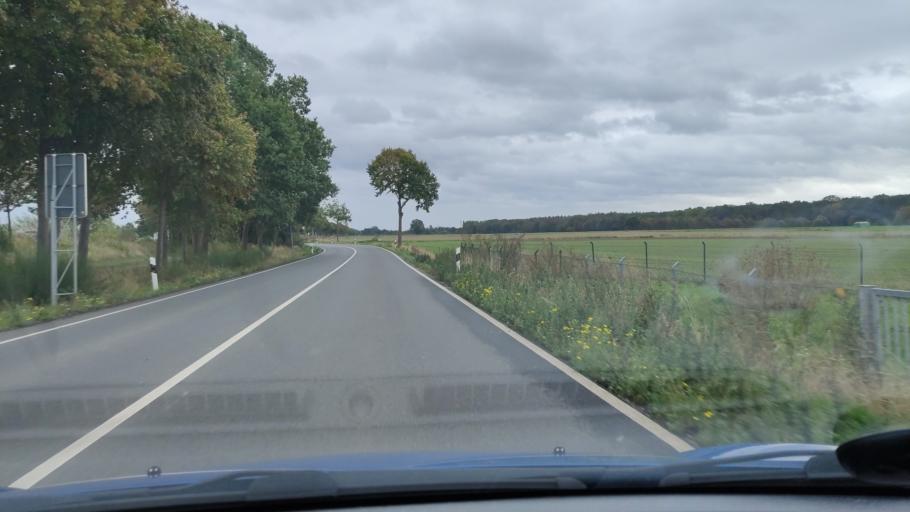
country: DE
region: Lower Saxony
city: Garbsen
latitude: 52.3972
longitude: 9.5523
